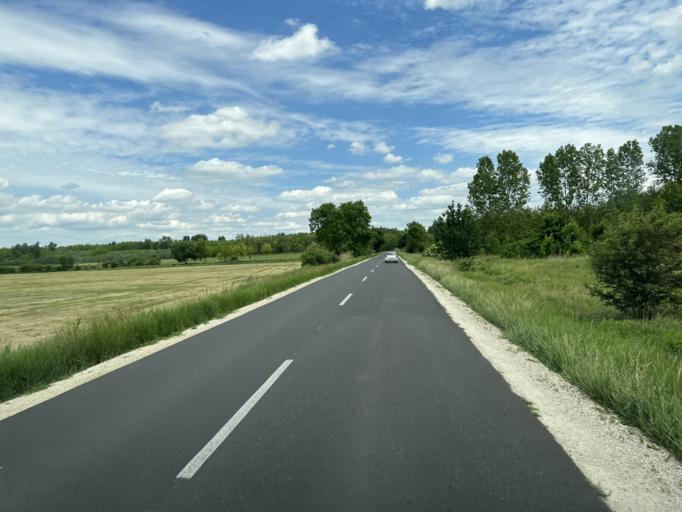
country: HU
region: Pest
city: Suelysap
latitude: 47.4660
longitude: 19.5568
